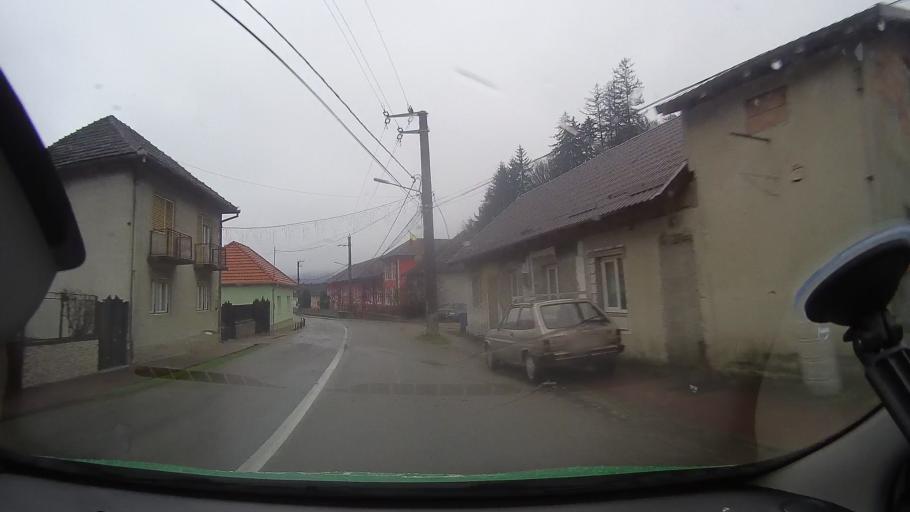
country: RO
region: Arad
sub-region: Comuna Moneasa
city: Moneasa
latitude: 46.4537
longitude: 22.2493
